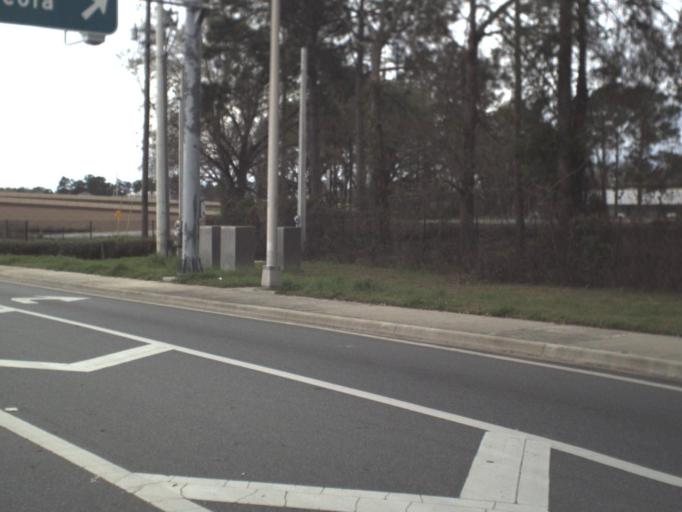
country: US
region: Florida
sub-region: Leon County
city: Tallahassee
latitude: 30.5036
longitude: -84.2516
